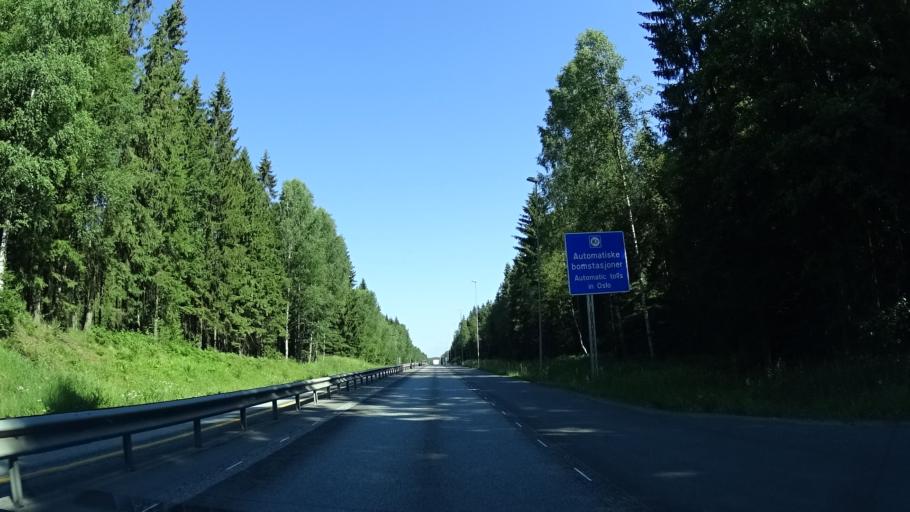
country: NO
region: Akershus
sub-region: Oppegard
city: Kolbotn
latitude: 59.7677
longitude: 10.7744
